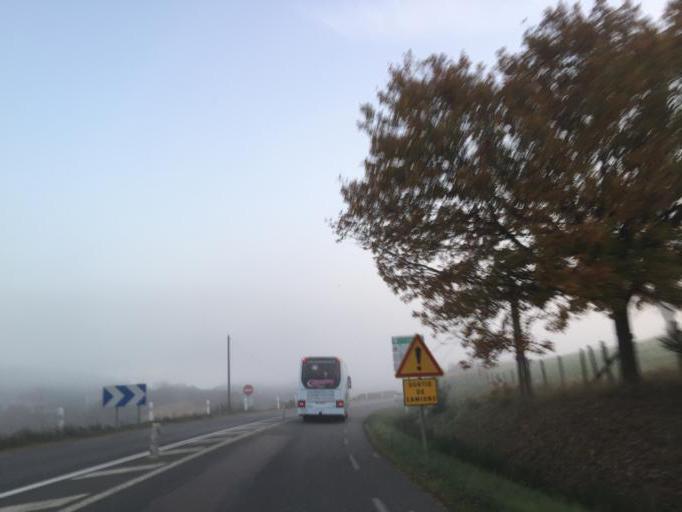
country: FR
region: Rhone-Alpes
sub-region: Departement de la Loire
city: Balbigny
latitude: 45.8579
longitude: 4.1730
